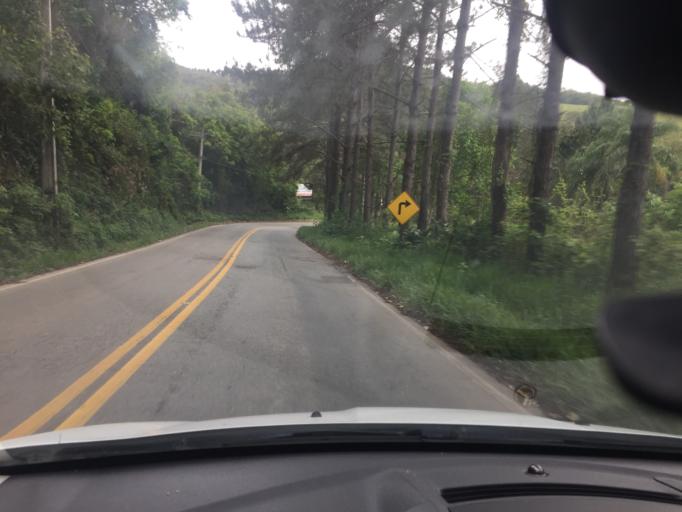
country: BR
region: Sao Paulo
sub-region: Jarinu
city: Jarinu
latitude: -23.1260
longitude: -46.7181
